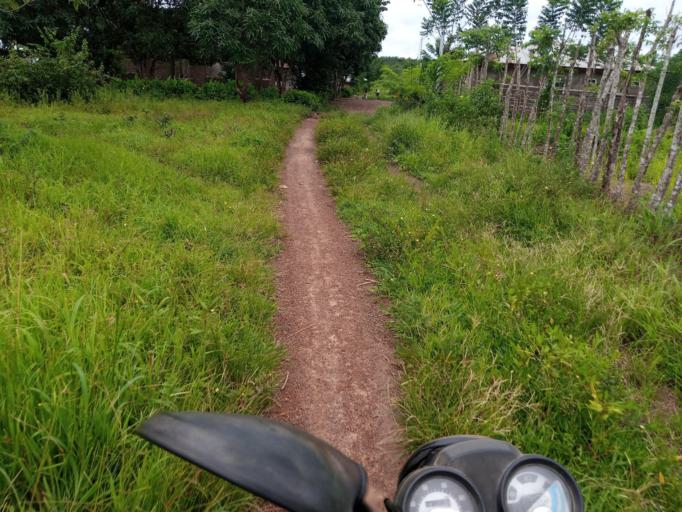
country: SL
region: Southern Province
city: Largo
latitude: 8.1923
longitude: -12.0611
